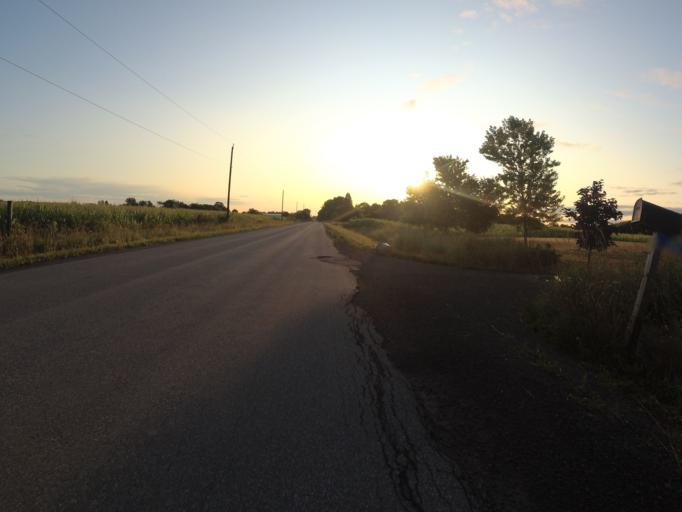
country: CA
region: Ontario
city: Ottawa
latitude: 45.1135
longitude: -75.5277
